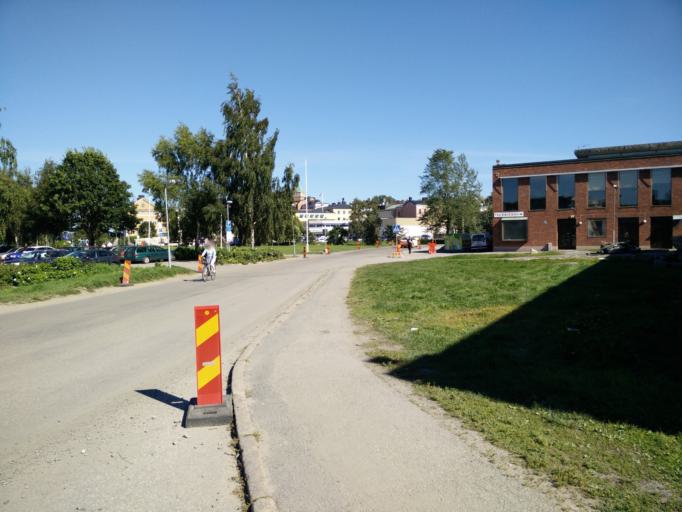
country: SE
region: Vaesternorrland
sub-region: Haernoesands Kommun
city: Haernoesand
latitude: 62.6303
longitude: 17.9354
